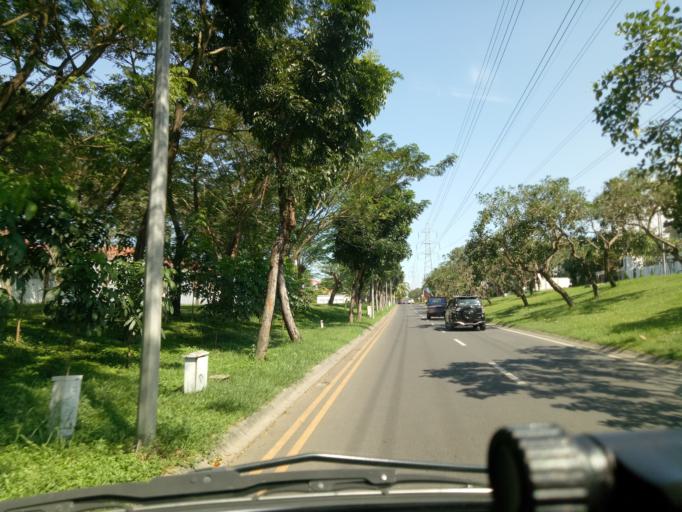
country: ID
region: East Java
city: Driyorejo
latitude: -7.2867
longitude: 112.6475
